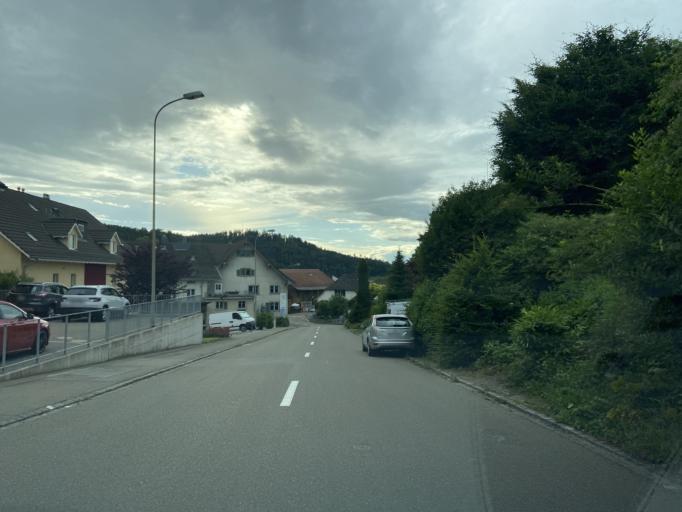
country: CH
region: Zurich
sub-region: Bezirk Winterthur
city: Elgg / Staedtchen und Umgebung
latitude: 47.4922
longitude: 8.8656
